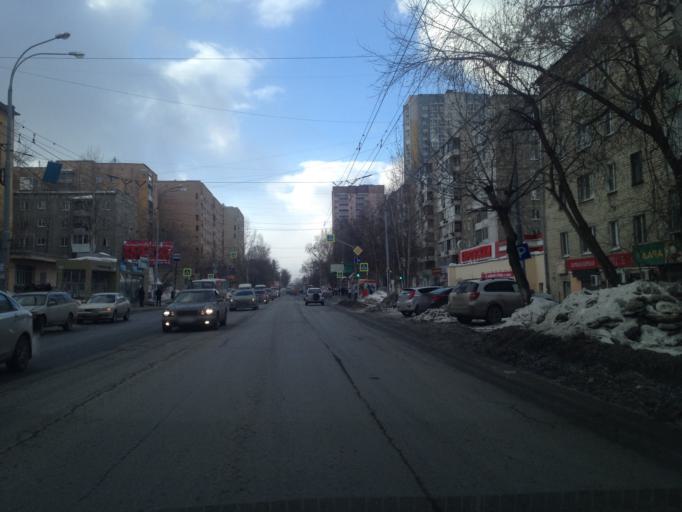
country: RU
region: Sverdlovsk
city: Yekaterinburg
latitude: 56.8617
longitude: 60.6402
